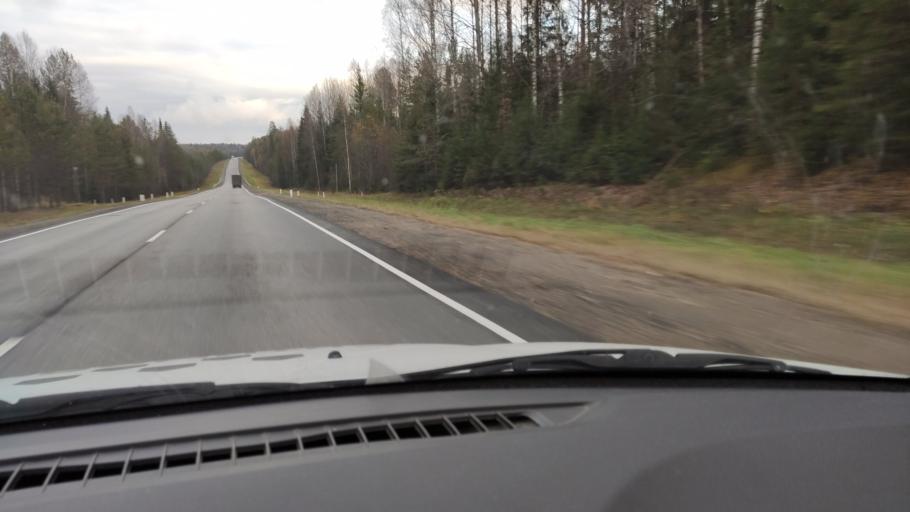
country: RU
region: Kirov
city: Chernaya Kholunitsa
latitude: 58.8268
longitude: 51.7798
